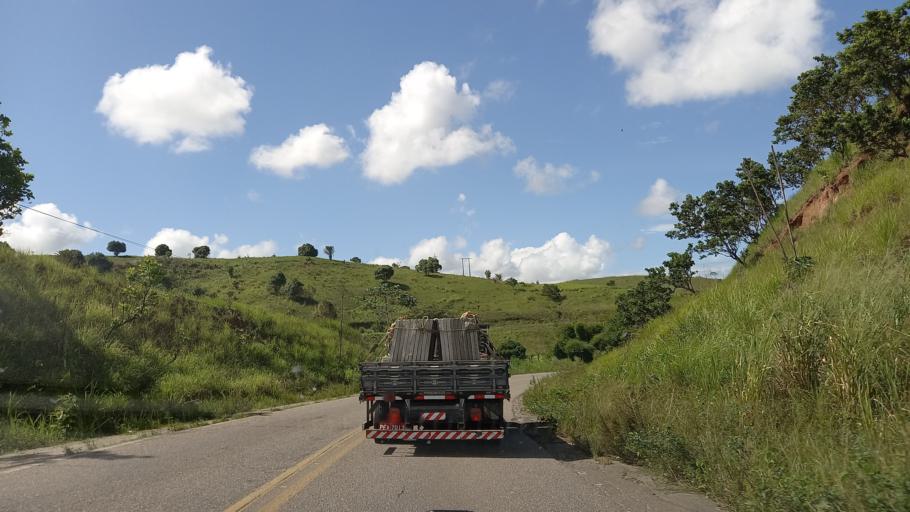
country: BR
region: Pernambuco
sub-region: Barreiros
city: Barreiros
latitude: -8.7851
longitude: -35.1836
